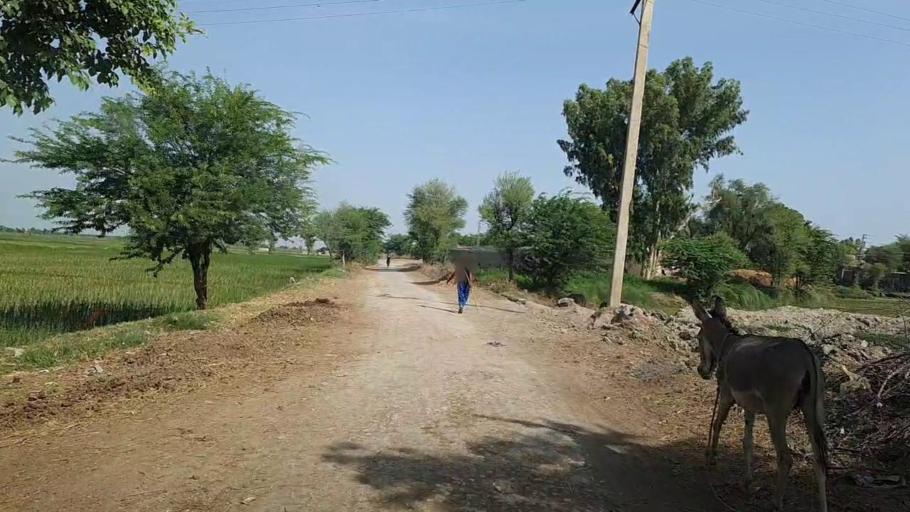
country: PK
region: Sindh
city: Mehar
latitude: 27.1180
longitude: 67.8408
